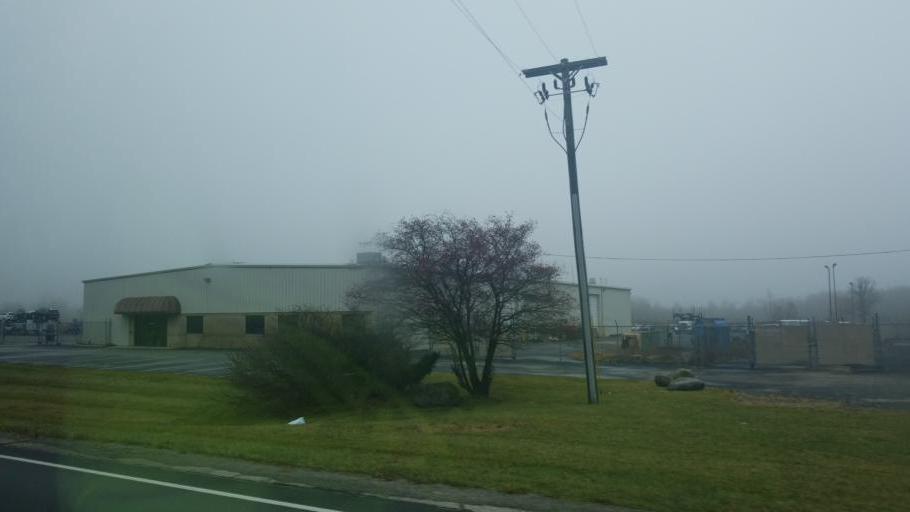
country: US
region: Ohio
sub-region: Union County
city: Marysville
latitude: 40.2614
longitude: -83.4621
